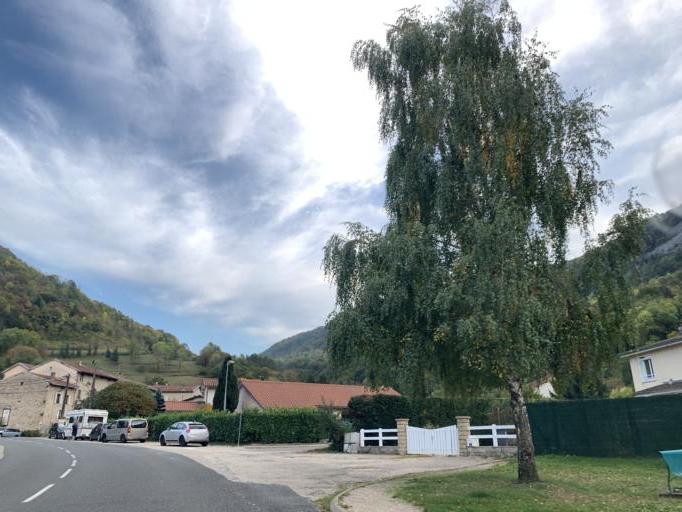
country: FR
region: Rhone-Alpes
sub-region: Departement de l'Ain
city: Saint-Rambert-en-Bugey
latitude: 45.9333
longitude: 5.4248
